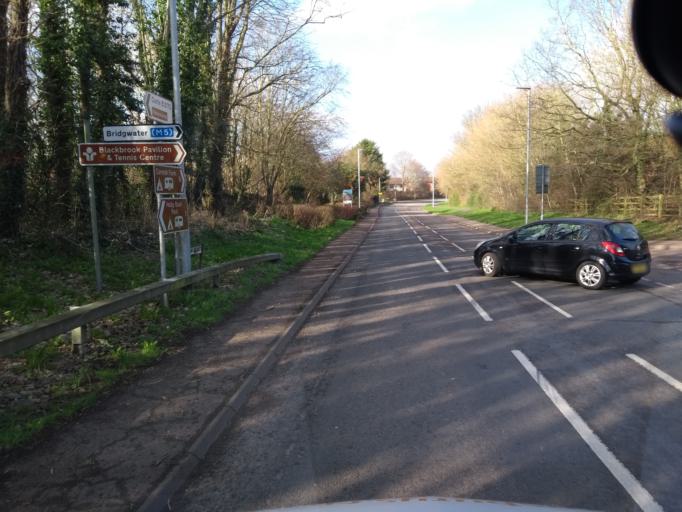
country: GB
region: England
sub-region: Somerset
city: Taunton
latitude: 50.9983
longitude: -3.0847
